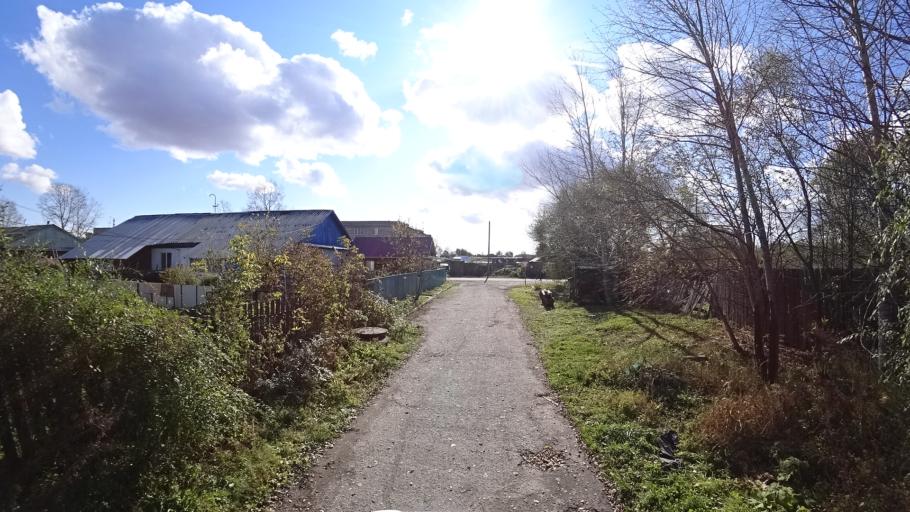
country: RU
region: Khabarovsk Krai
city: Amursk
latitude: 50.0991
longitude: 136.5009
